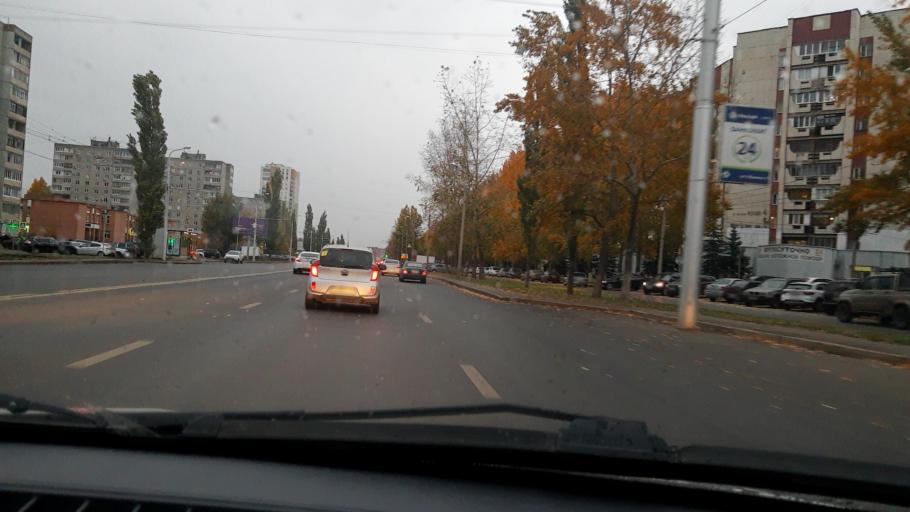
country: RU
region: Bashkortostan
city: Ufa
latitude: 54.7661
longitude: 56.0504
